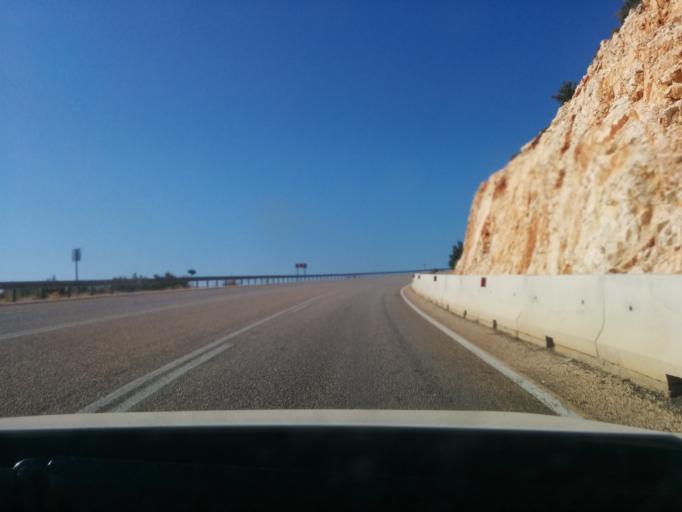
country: TR
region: Antalya
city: Kalkan
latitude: 36.2701
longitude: 29.4059
